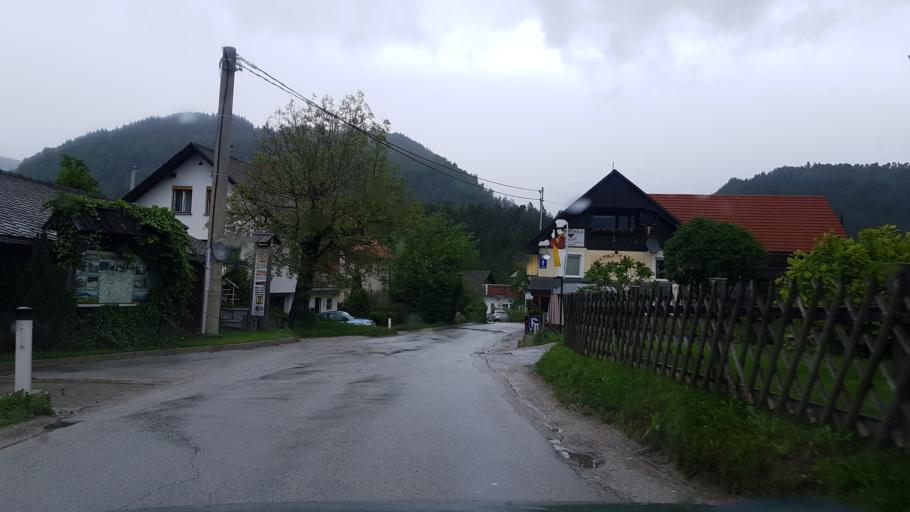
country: SI
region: Gorje
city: Zgornje Gorje
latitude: 46.3870
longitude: 14.0776
